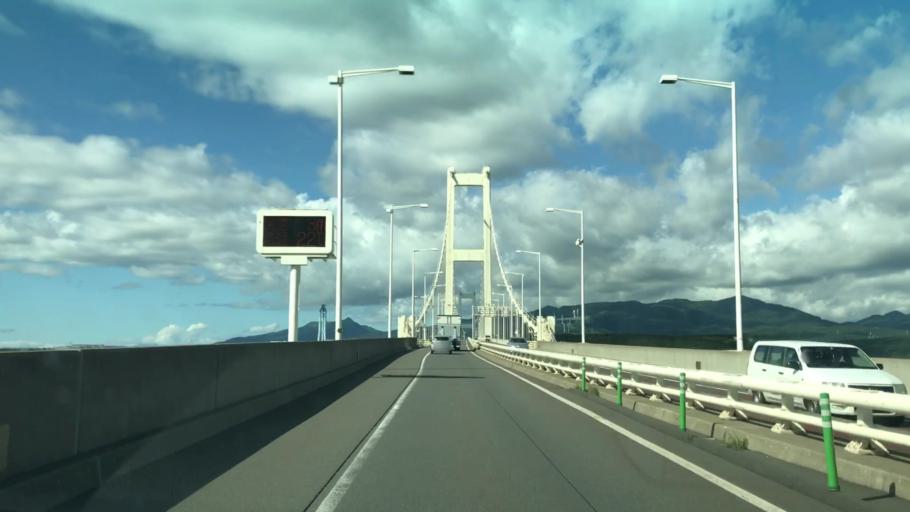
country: JP
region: Hokkaido
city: Muroran
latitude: 42.3457
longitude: 140.9490
